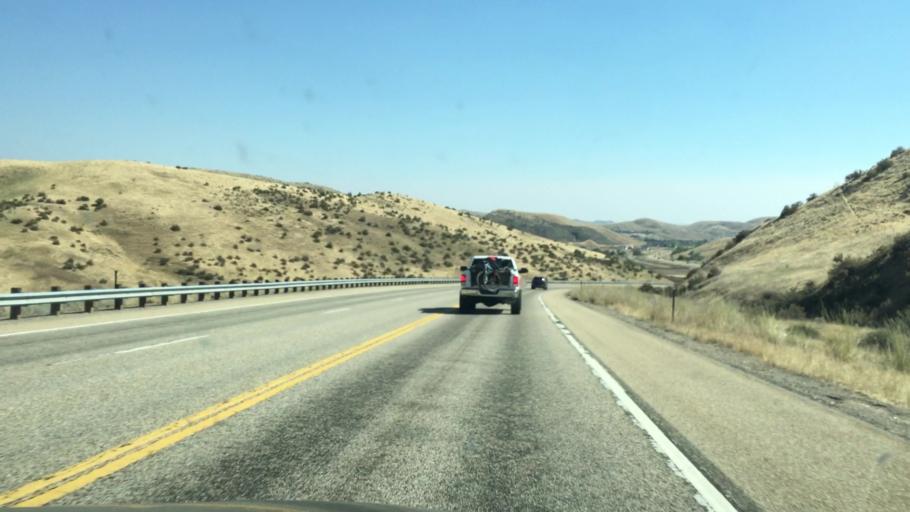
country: US
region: Idaho
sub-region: Ada County
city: Eagle
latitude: 43.8047
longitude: -116.2647
